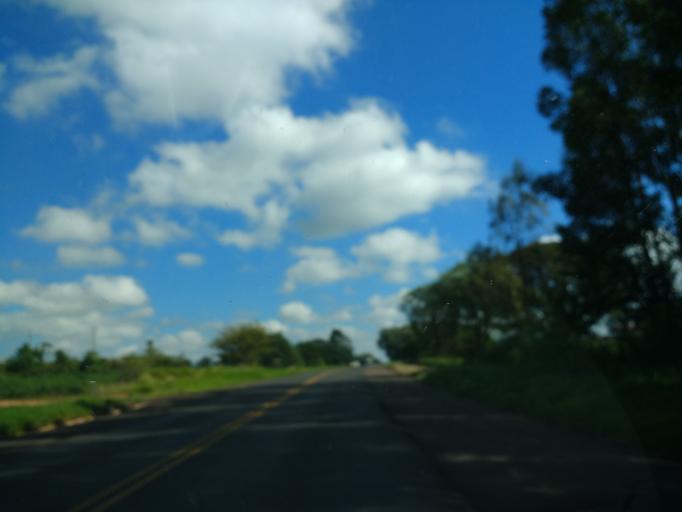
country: BR
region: Parana
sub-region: Umuarama
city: Umuarama
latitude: -23.8531
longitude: -53.3729
